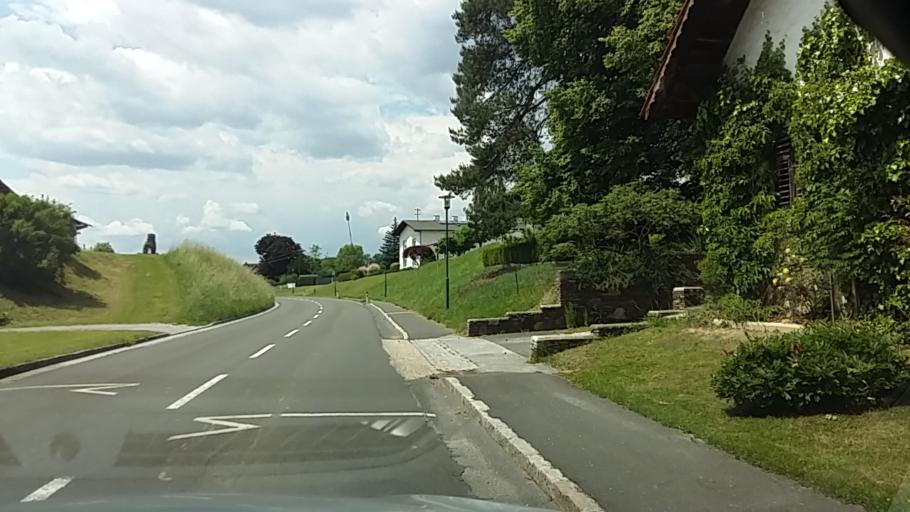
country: AT
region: Styria
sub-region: Politischer Bezirk Hartberg-Fuerstenfeld
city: Ilz
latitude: 47.0882
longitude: 15.9438
